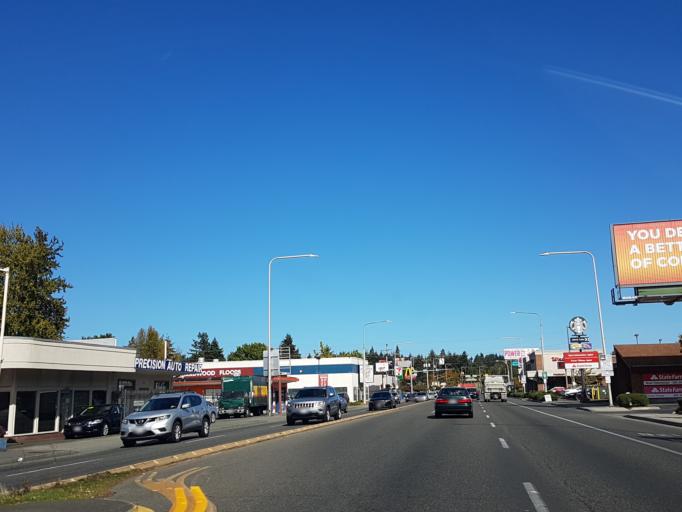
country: US
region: Washington
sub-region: King County
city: Lake Forest Park
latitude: 47.7320
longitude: -122.2923
